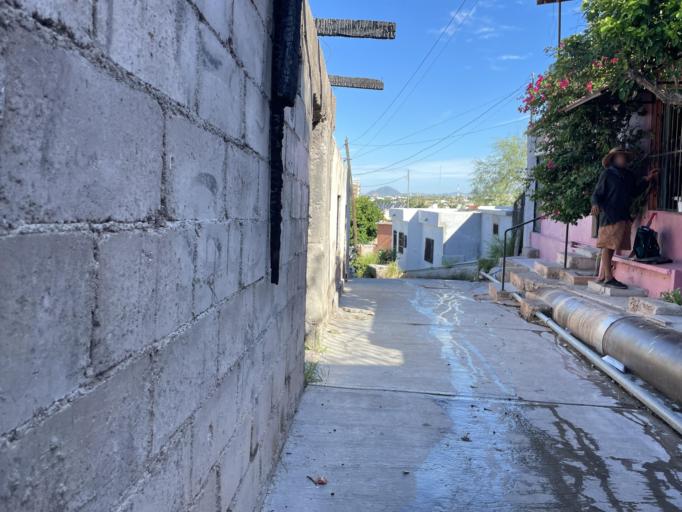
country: MX
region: Sonora
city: Hermosillo
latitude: 29.0744
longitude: -110.9536
